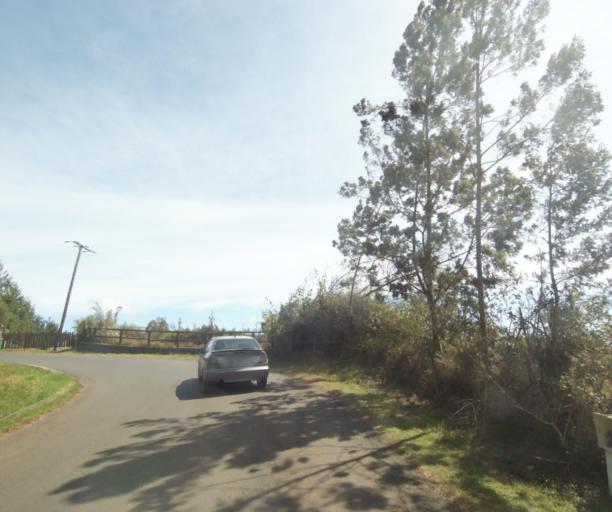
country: RE
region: Reunion
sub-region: Reunion
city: Trois-Bassins
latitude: -21.0467
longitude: 55.3327
